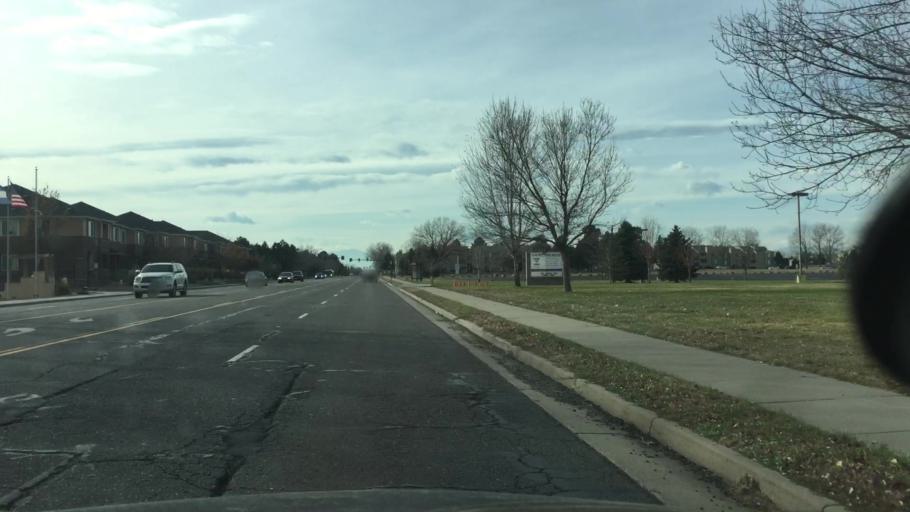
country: US
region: Colorado
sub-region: Arapahoe County
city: Glendale
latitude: 39.6894
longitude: -104.8785
